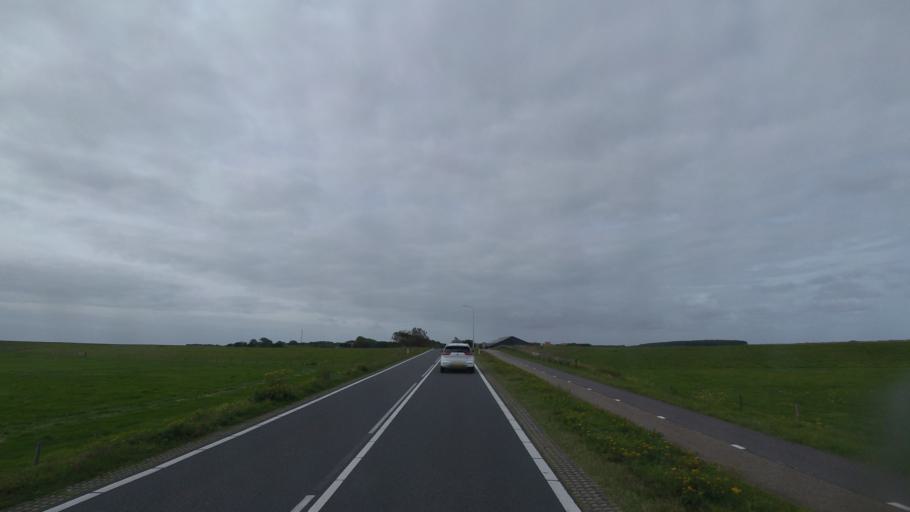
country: NL
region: Friesland
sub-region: Gemeente Ameland
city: Nes
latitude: 53.4460
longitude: 5.7342
